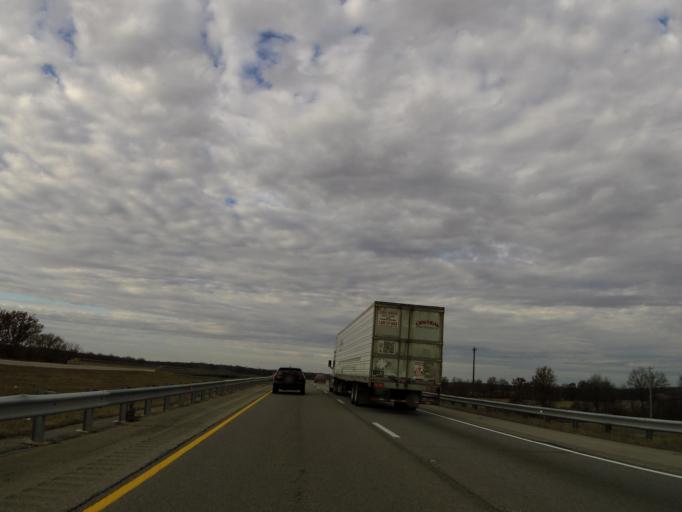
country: US
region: Illinois
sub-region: Clinton County
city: Wamac
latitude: 38.3623
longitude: -89.0699
